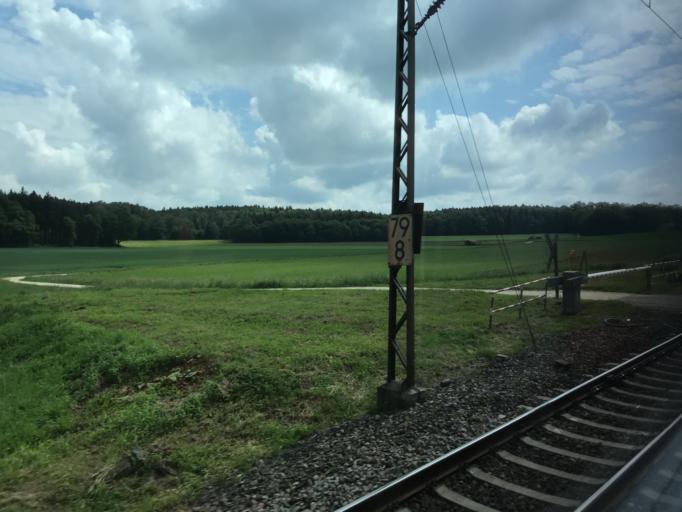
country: DE
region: Baden-Wuerttemberg
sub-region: Tuebingen Region
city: Beimerstetten
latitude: 48.4969
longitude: 9.9649
